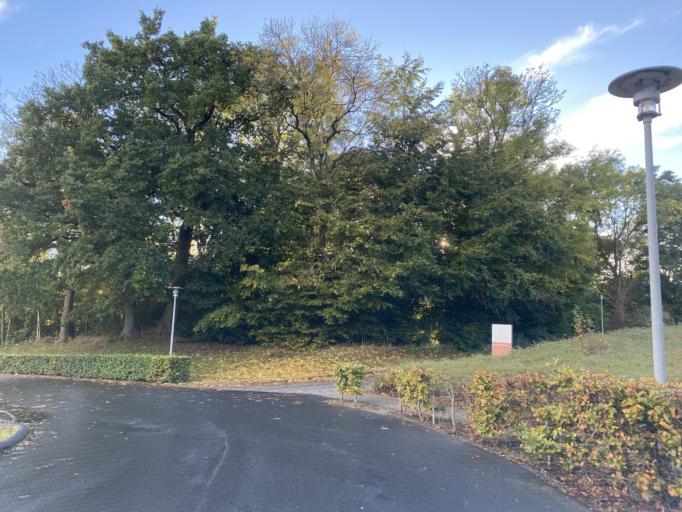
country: DK
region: South Denmark
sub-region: Haderslev Kommune
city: Haderslev
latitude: 55.2453
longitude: 9.4474
